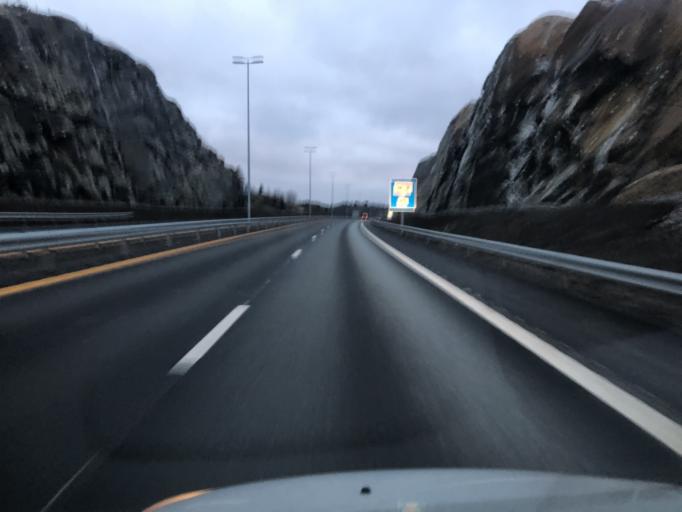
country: NO
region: Aust-Agder
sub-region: Arendal
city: Arendal
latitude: 58.5054
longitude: 8.8136
